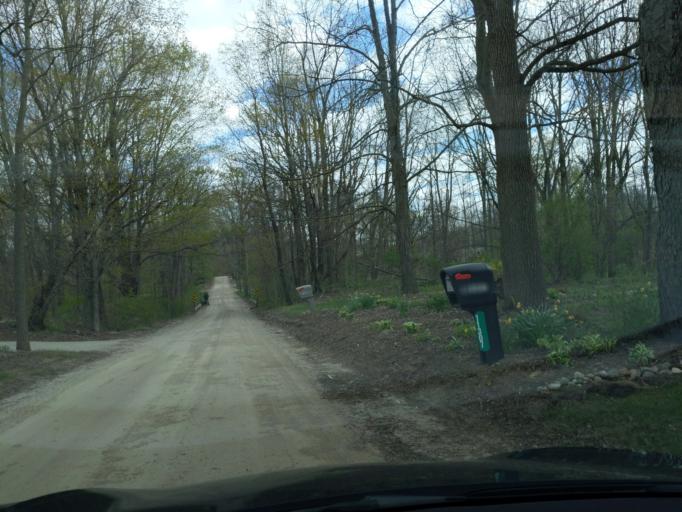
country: US
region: Michigan
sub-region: Eaton County
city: Dimondale
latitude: 42.6302
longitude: -84.6148
